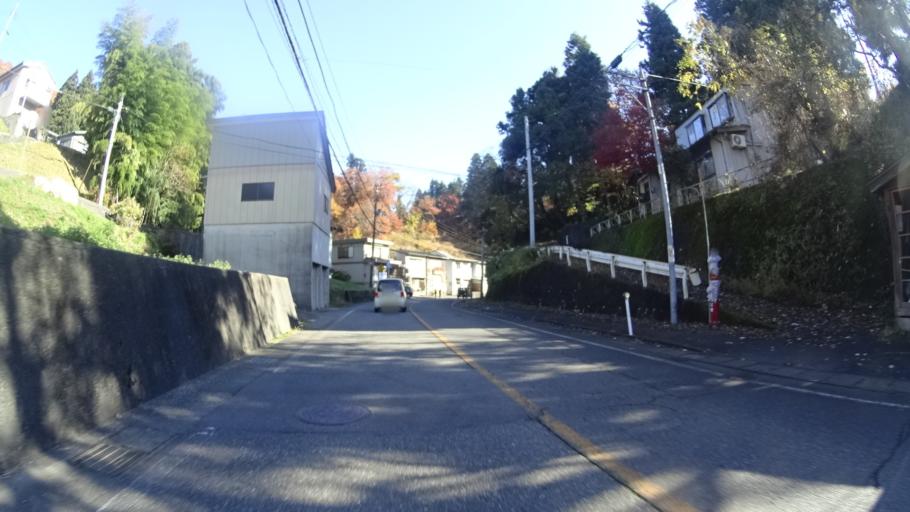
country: JP
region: Niigata
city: Tochio-honcho
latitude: 37.4831
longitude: 138.9874
